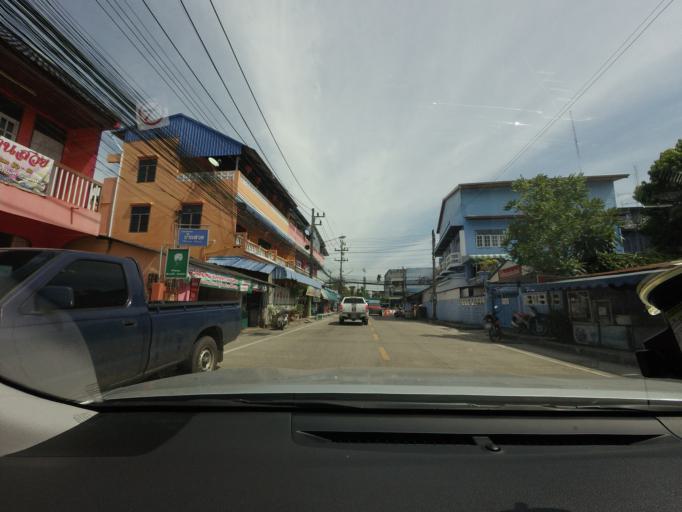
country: TH
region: Narathiwat
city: Narathiwat
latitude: 6.4215
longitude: 101.8180
